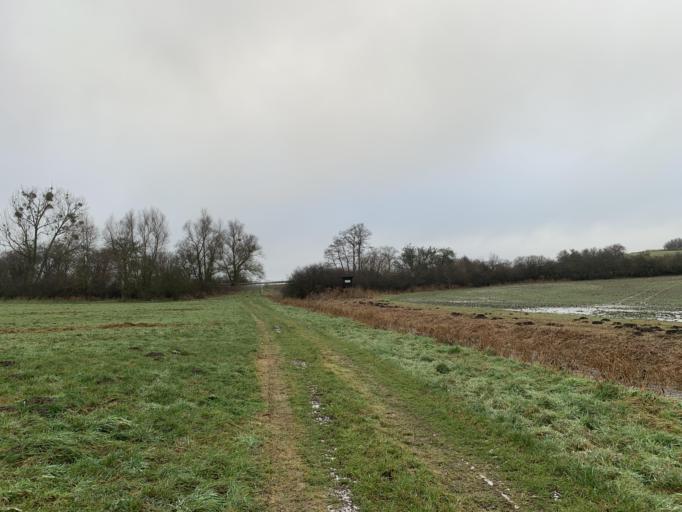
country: DE
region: Mecklenburg-Vorpommern
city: Blankensee
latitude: 53.4028
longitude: 13.2792
